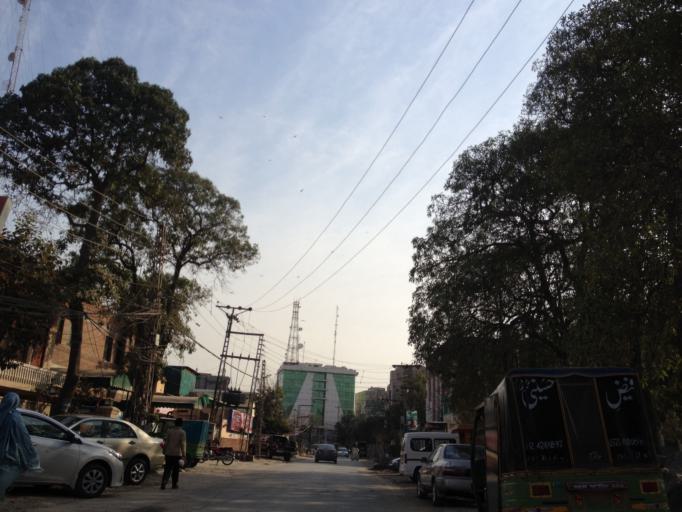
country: PK
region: Punjab
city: Lahore
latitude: 31.5026
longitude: 74.3191
